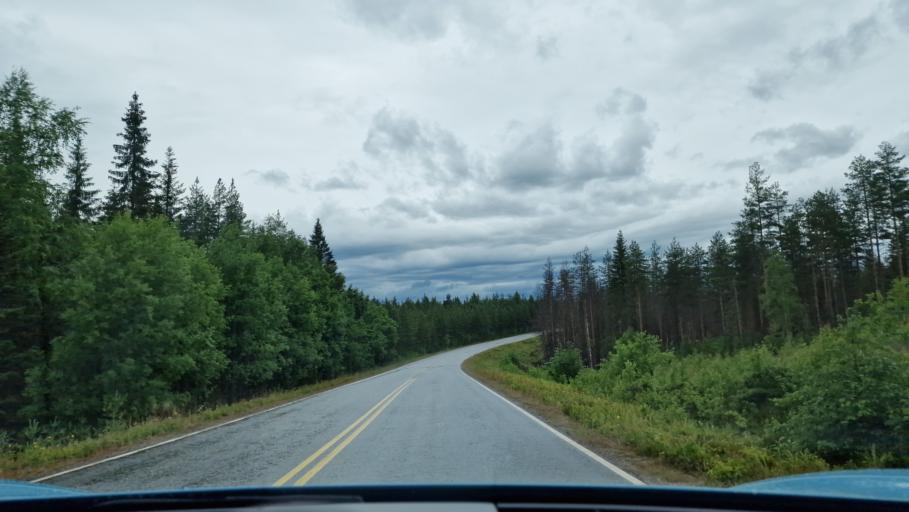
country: FI
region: Central Finland
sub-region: Saarijaervi-Viitasaari
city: Pylkoenmaeki
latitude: 62.6649
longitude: 24.5447
